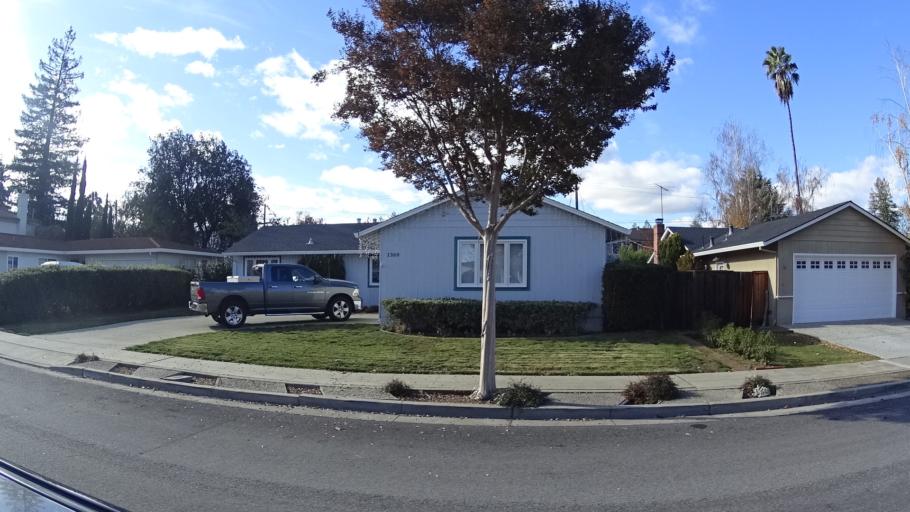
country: US
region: California
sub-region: Santa Clara County
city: Sunnyvale
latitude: 37.3491
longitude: -122.0542
